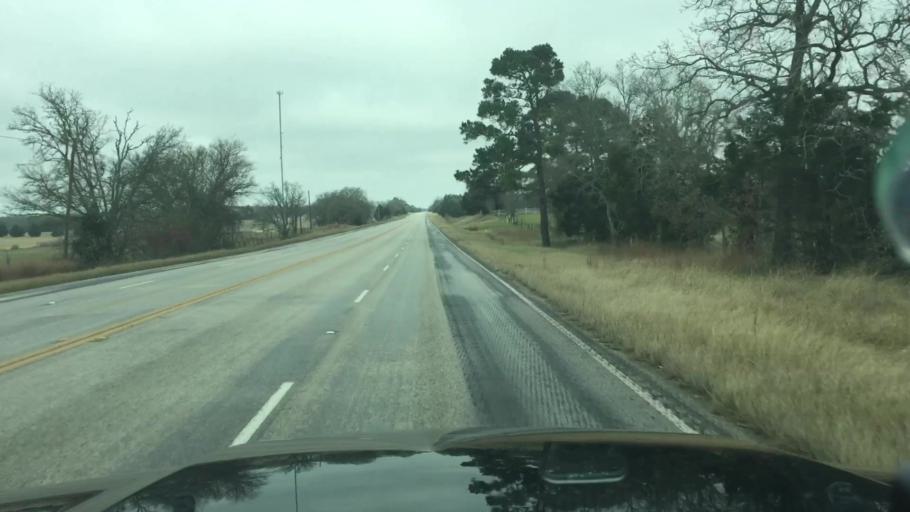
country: US
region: Texas
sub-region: Lee County
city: Giddings
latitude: 30.1033
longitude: -96.9140
